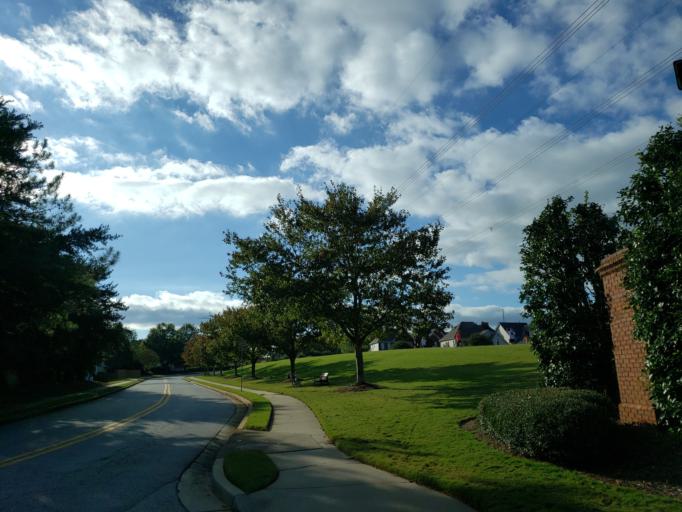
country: US
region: Georgia
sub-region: Cobb County
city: Marietta
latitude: 33.9885
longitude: -84.5042
